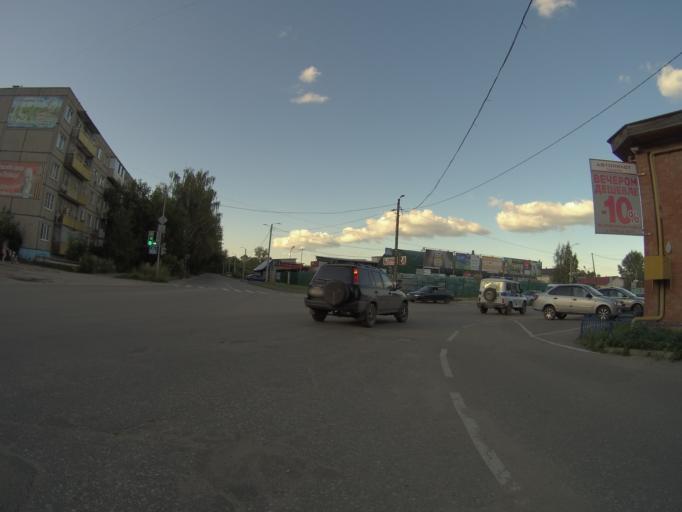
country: RU
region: Vladimir
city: Gus'-Khrustal'nyy
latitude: 55.6113
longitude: 40.6595
